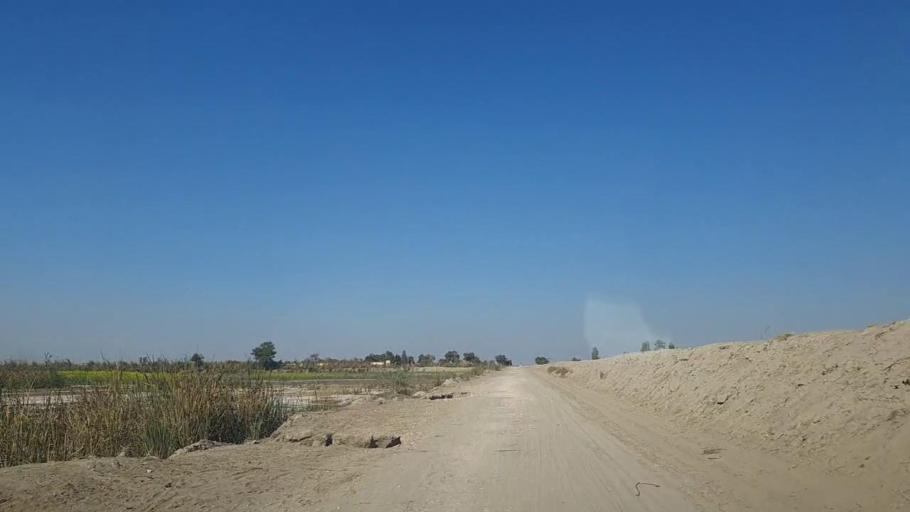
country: PK
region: Sindh
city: Sanghar
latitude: 26.2187
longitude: 68.9291
